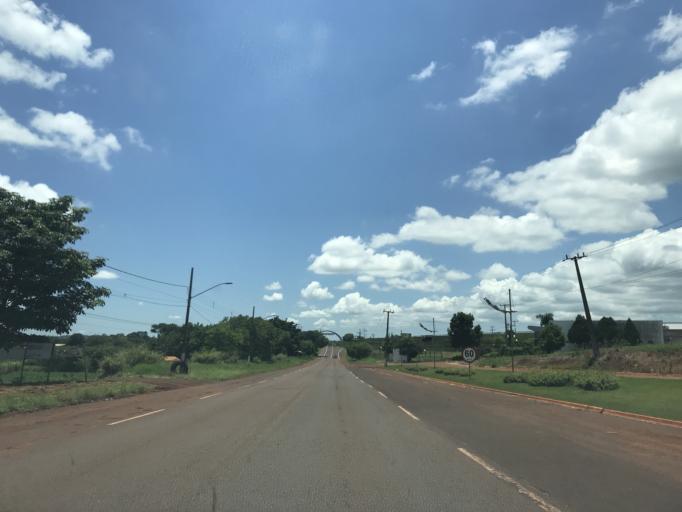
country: BR
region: Parana
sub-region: Marialva
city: Marialva
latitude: -23.4979
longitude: -51.7751
